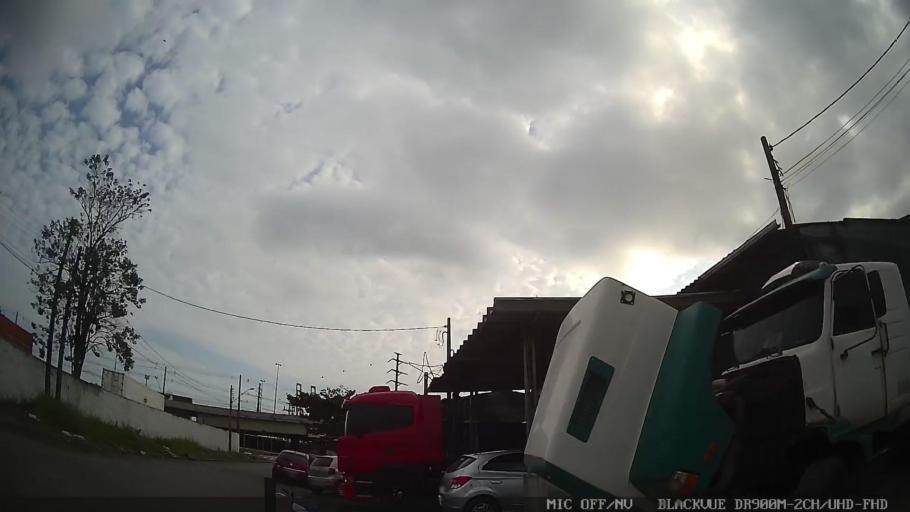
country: BR
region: Sao Paulo
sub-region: Guaruja
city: Guaruja
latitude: -23.9634
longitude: -46.2832
